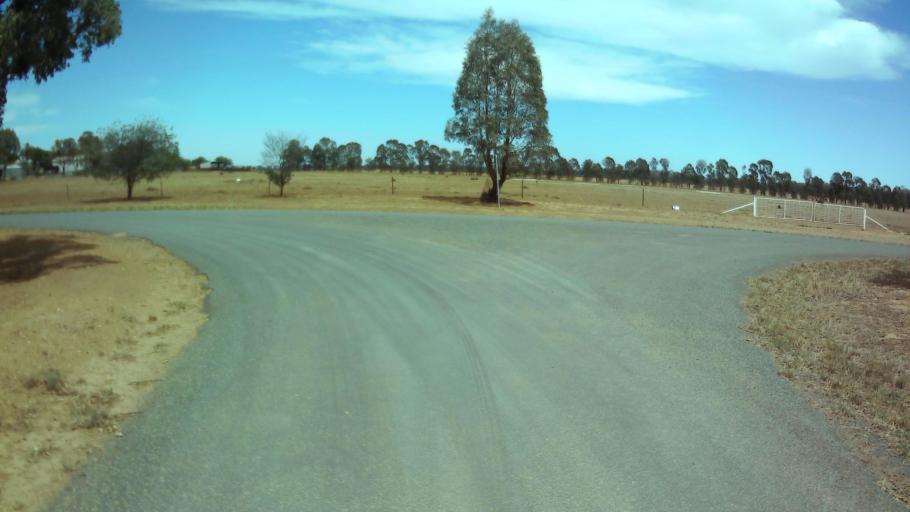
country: AU
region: New South Wales
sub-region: Weddin
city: Grenfell
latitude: -33.8562
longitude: 147.9038
